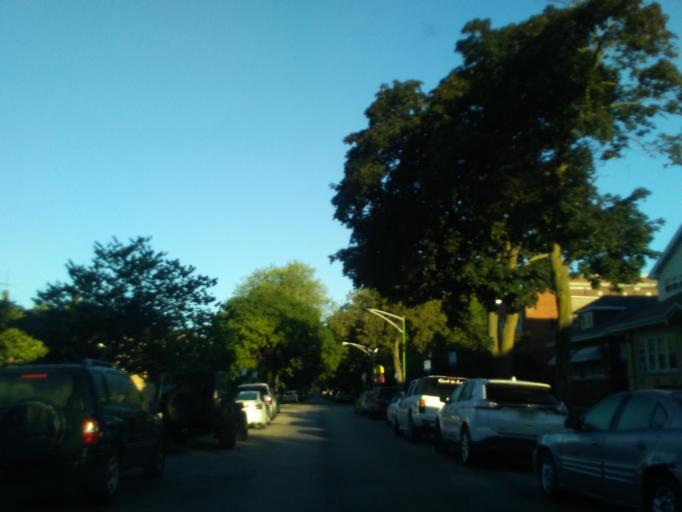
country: US
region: Illinois
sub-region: Cook County
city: Oak Park
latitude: 41.9352
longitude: -87.7485
